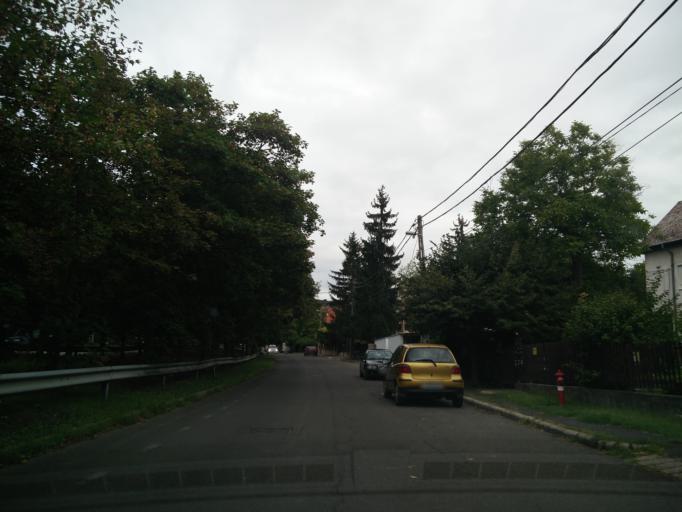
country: HU
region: Budapest
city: Budapest XII. keruelet
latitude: 47.4736
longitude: 19.0032
